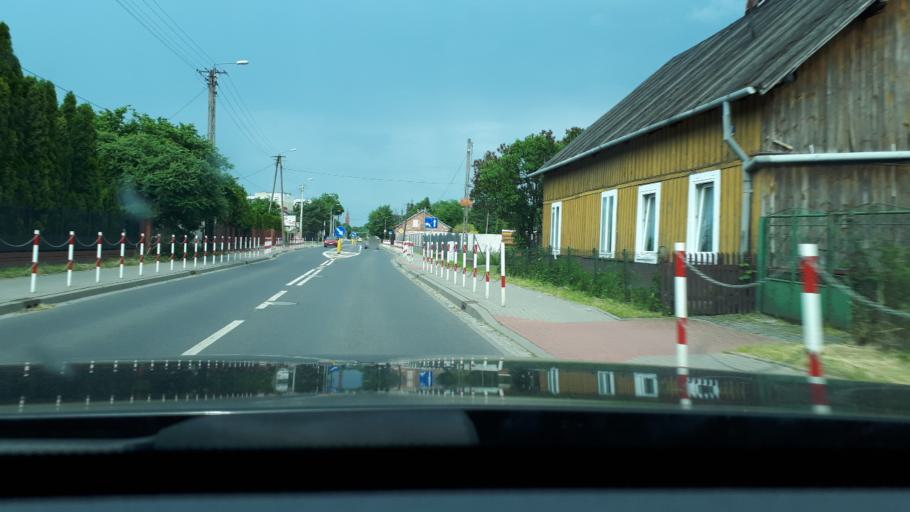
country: PL
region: Masovian Voivodeship
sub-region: Powiat warszawski zachodni
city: Leszno
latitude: 52.2574
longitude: 20.5759
